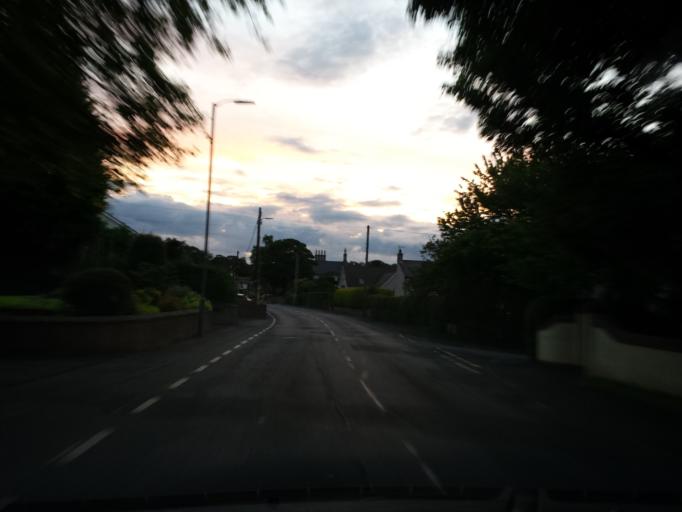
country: GB
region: Scotland
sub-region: The Scottish Borders
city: Eyemouth
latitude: 55.8846
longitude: -2.1557
